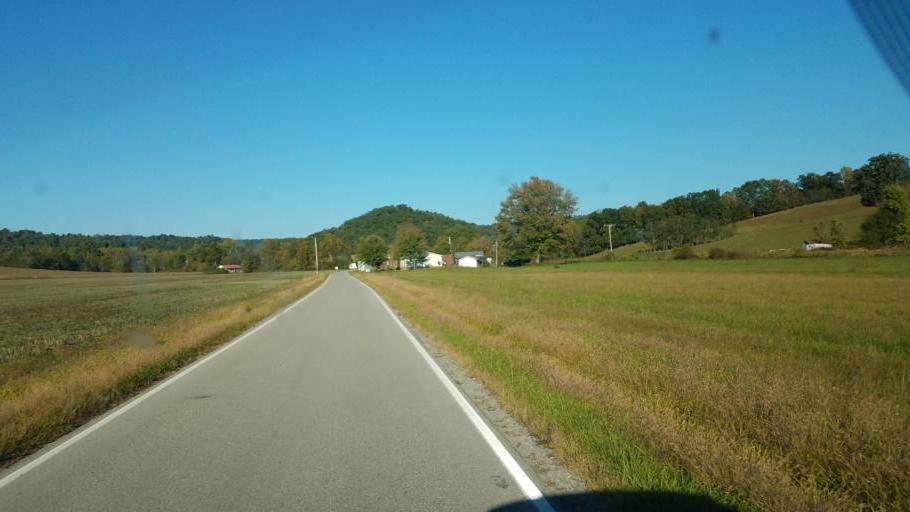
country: US
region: Ohio
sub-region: Adams County
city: Manchester
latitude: 38.5066
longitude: -83.5452
